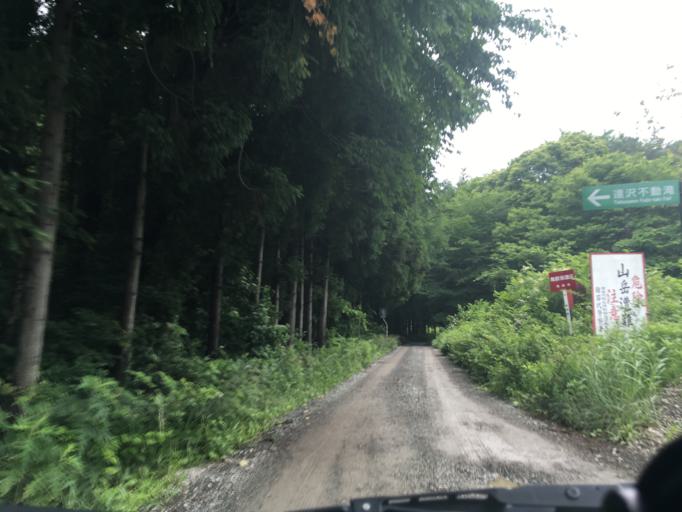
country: JP
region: Fukushima
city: Inawashiro
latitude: 37.5877
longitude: 140.2229
